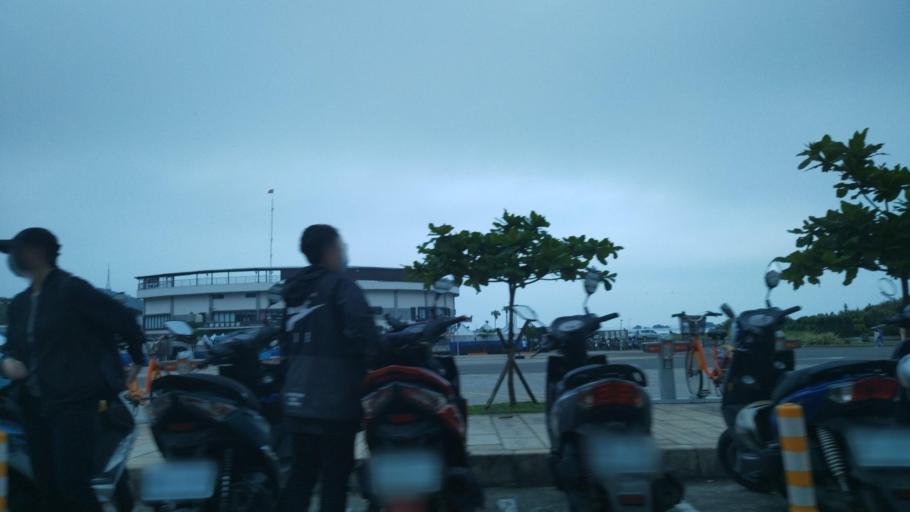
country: TW
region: Taiwan
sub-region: Keelung
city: Keelung
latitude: 25.2044
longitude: 121.6903
